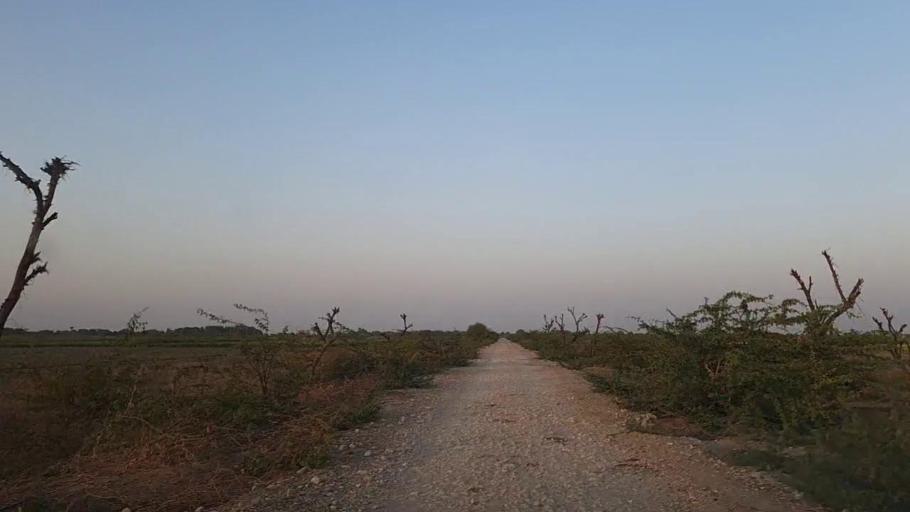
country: PK
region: Sindh
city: Naukot
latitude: 24.8764
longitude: 69.3506
